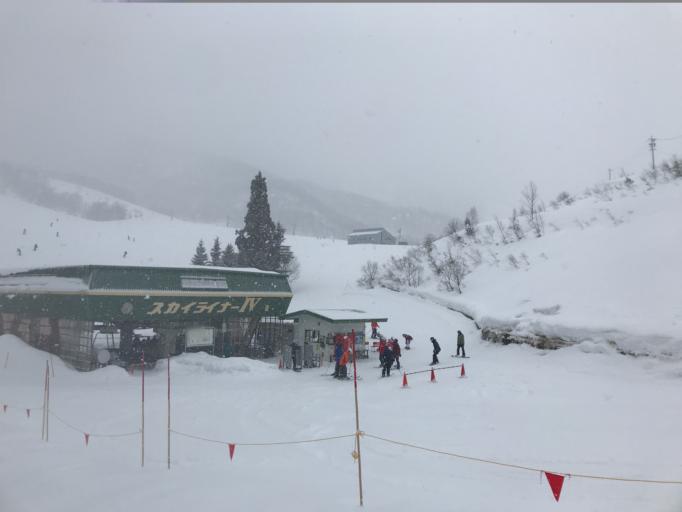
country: JP
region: Nagano
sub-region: Kitaazumi Gun
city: Hakuba
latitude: 36.7485
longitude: 137.8594
